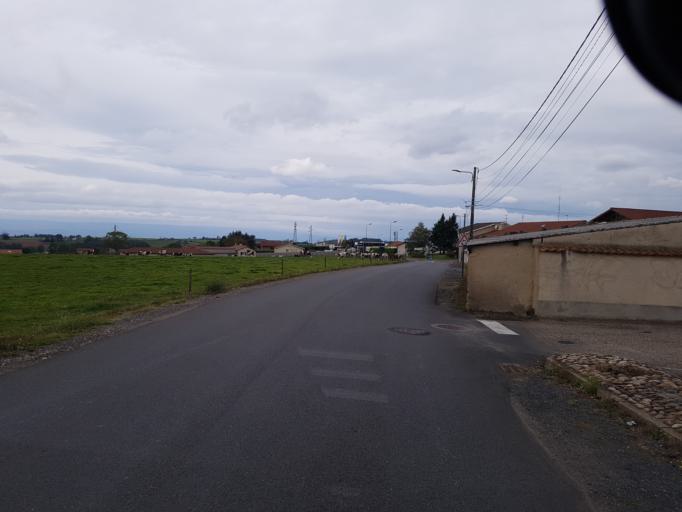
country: FR
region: Rhone-Alpes
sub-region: Departement de la Loire
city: Chazelles-sur-Lyon
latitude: 45.6347
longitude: 4.3808
